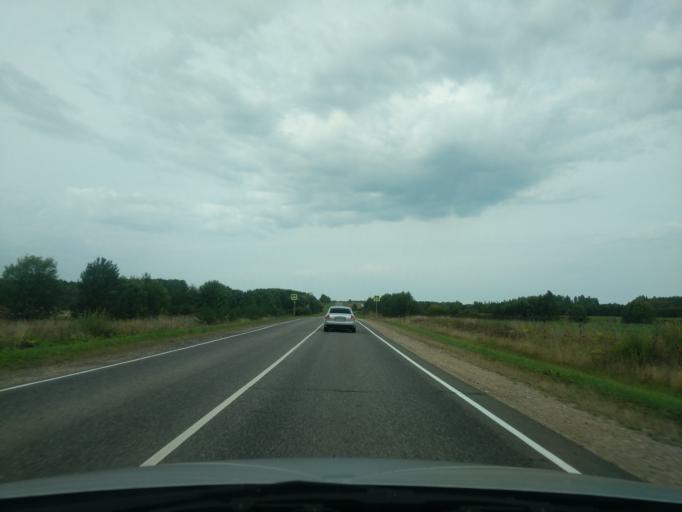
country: RU
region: Kirov
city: Mirnyy
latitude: 58.2727
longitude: 47.7866
